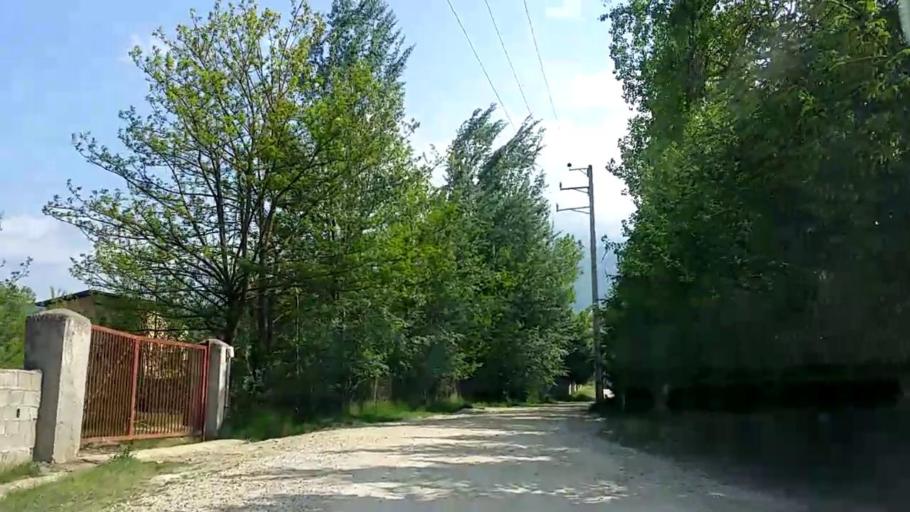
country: IR
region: Mazandaran
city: `Abbasabad
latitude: 36.5251
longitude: 51.1830
